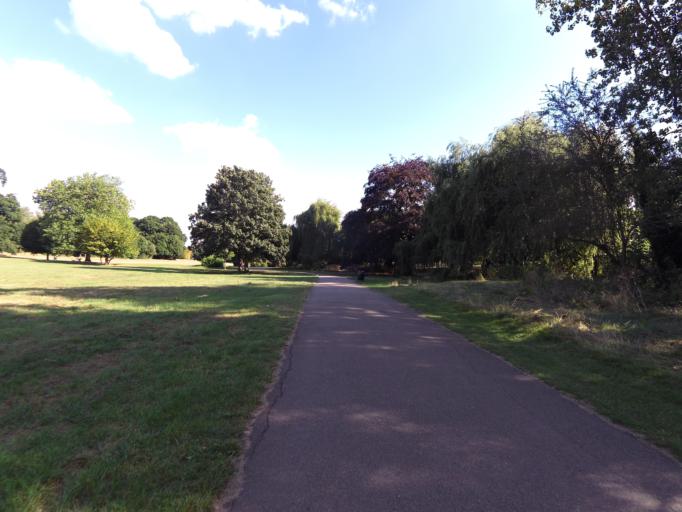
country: GB
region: England
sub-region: Greater London
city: Wood Green
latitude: 51.6200
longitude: -0.1342
